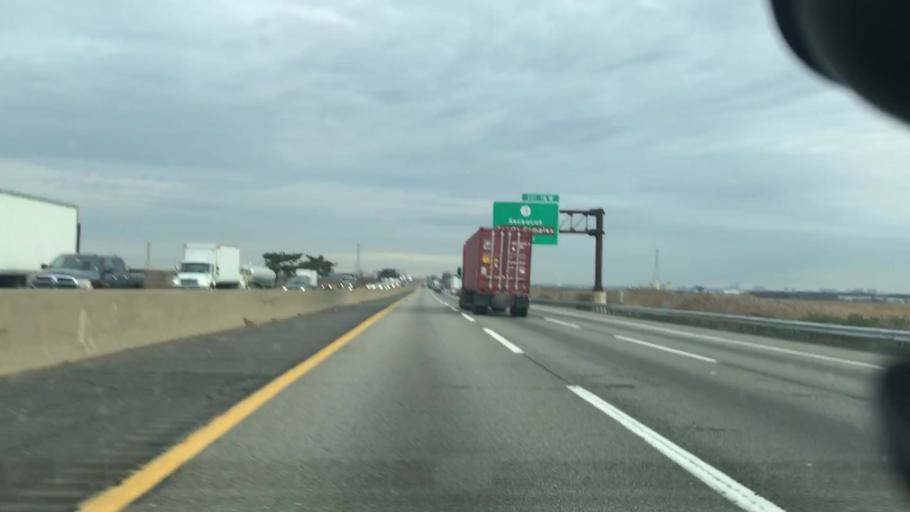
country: US
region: New Jersey
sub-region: Bergen County
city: North Arlington
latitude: 40.7757
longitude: -74.1016
